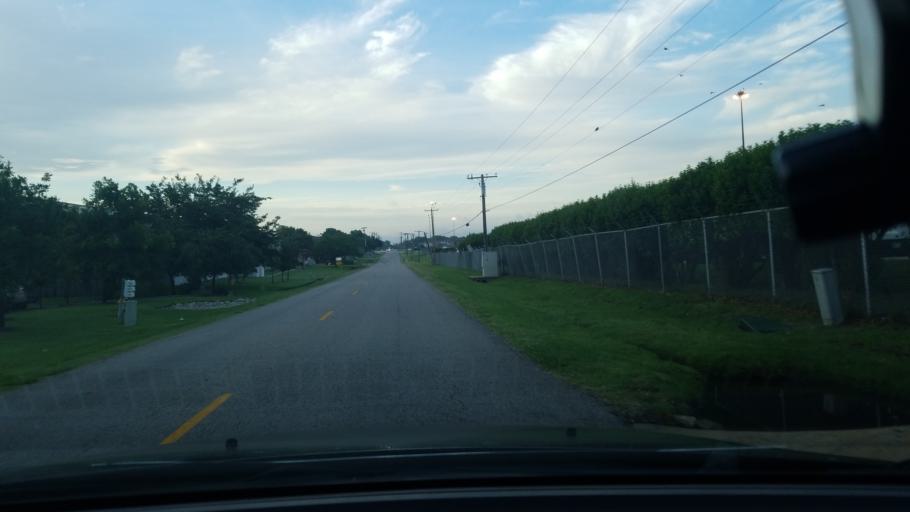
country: US
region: Texas
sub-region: Dallas County
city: Balch Springs
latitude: 32.7713
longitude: -96.6536
